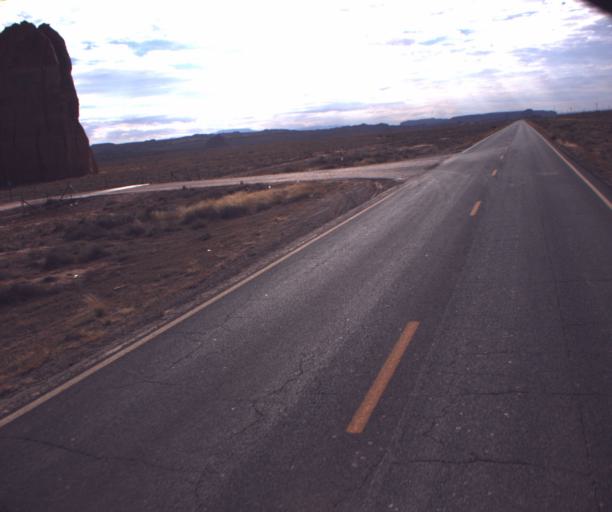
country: US
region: Arizona
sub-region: Apache County
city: Many Farms
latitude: 36.7478
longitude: -109.6415
